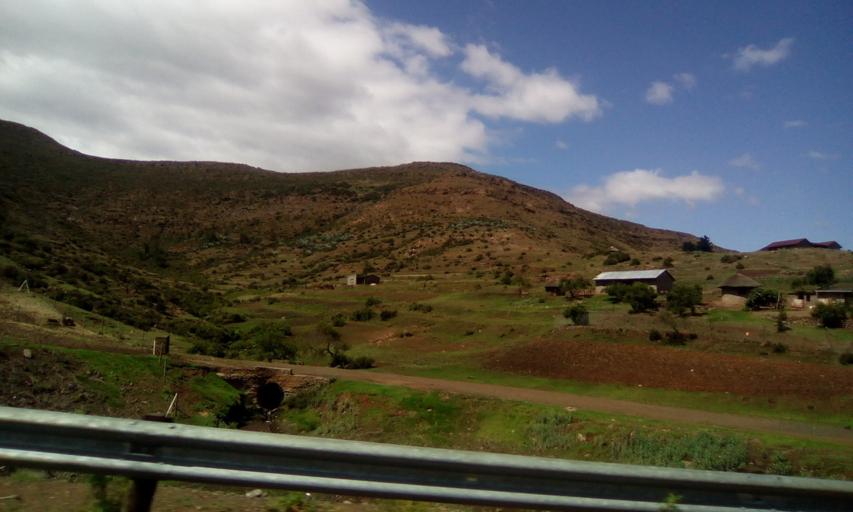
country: LS
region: Maseru
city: Nako
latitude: -29.6564
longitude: 27.8331
